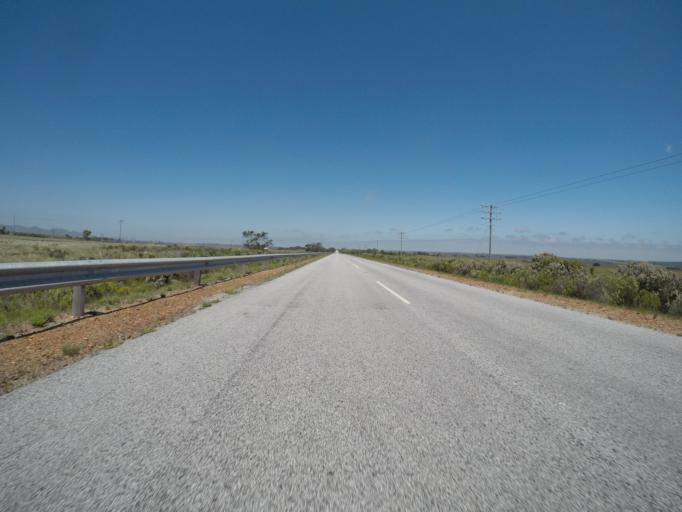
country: ZA
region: Eastern Cape
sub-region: Cacadu District Municipality
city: Kruisfontein
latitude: -34.0039
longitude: 24.5511
